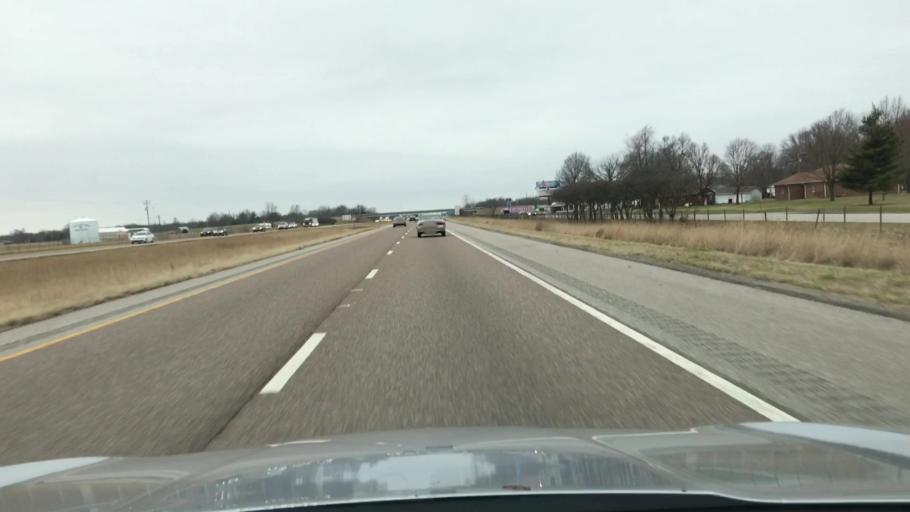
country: US
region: Illinois
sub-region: Macoupin County
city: Staunton
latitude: 38.9631
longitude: -89.7597
